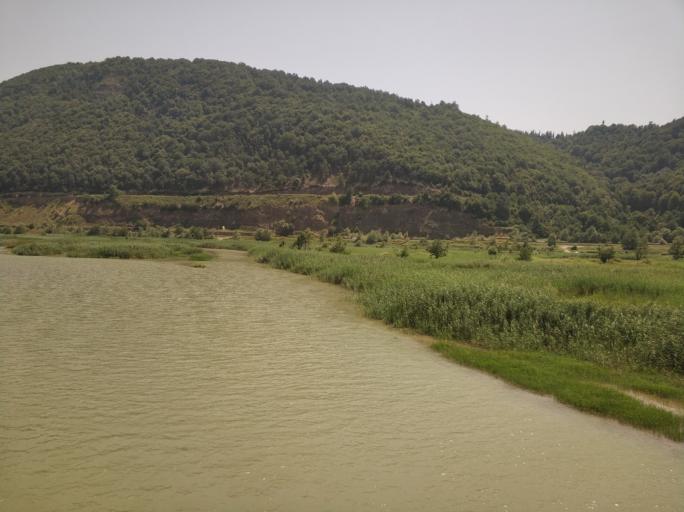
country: IR
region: Gilan
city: Pa'in-e Bazar-e Rudbar
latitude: 36.9749
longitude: 49.5536
